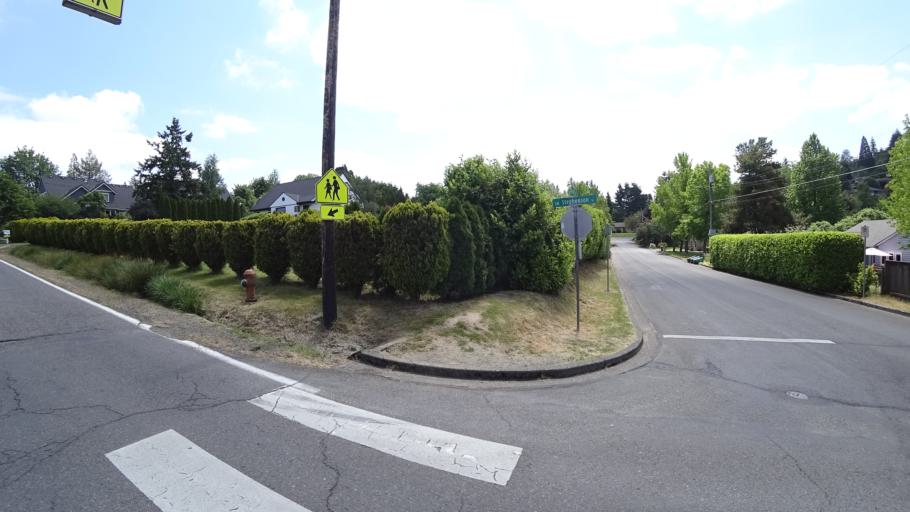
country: US
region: Oregon
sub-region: Clackamas County
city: Lake Oswego
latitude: 45.4402
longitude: -122.7050
